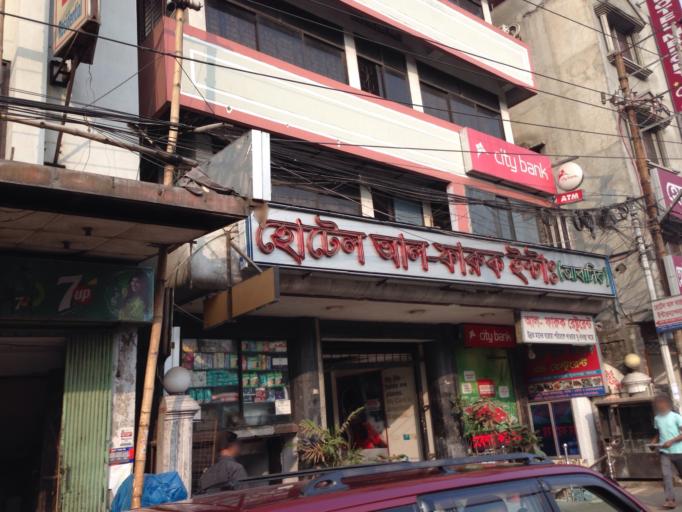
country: BD
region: Dhaka
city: Paltan
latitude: 23.7310
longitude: 90.4252
